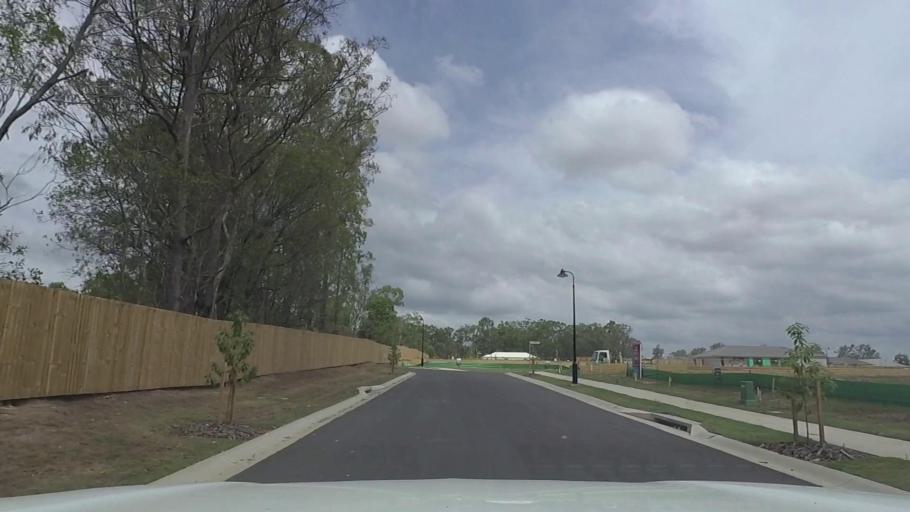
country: AU
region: Queensland
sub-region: Logan
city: Waterford West
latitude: -27.7017
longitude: 153.1087
